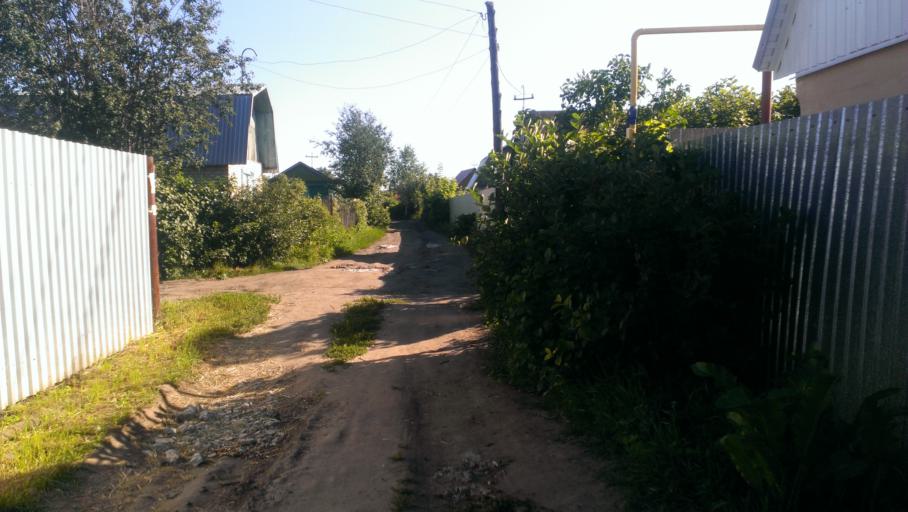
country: RU
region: Altai Krai
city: Novosilikatnyy
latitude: 53.3239
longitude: 83.6695
